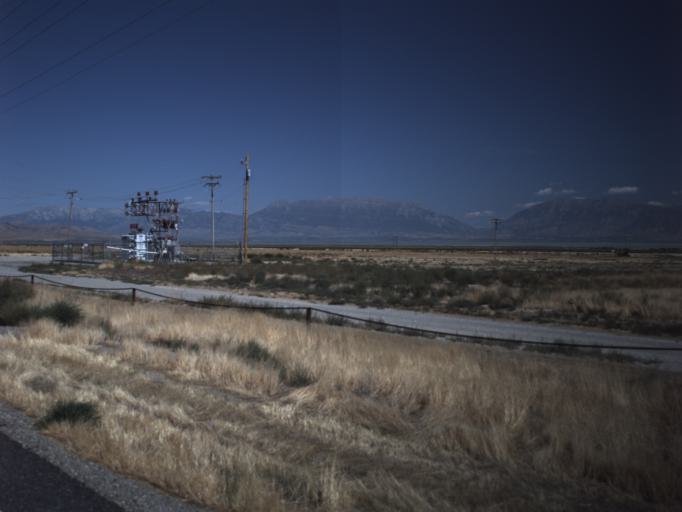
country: US
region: Utah
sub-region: Utah County
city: Genola
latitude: 40.0749
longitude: -111.9586
